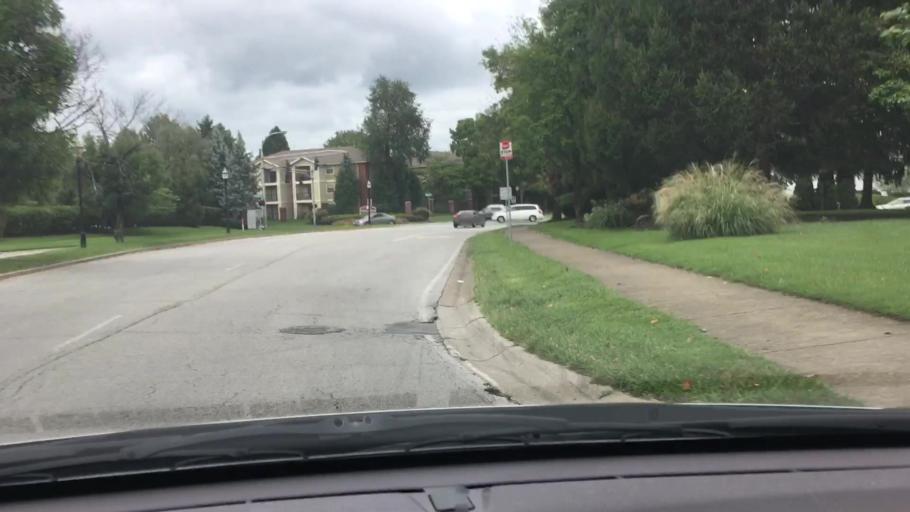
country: US
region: Kentucky
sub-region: Jefferson County
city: Beechwood Village
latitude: 38.2409
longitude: -85.6360
